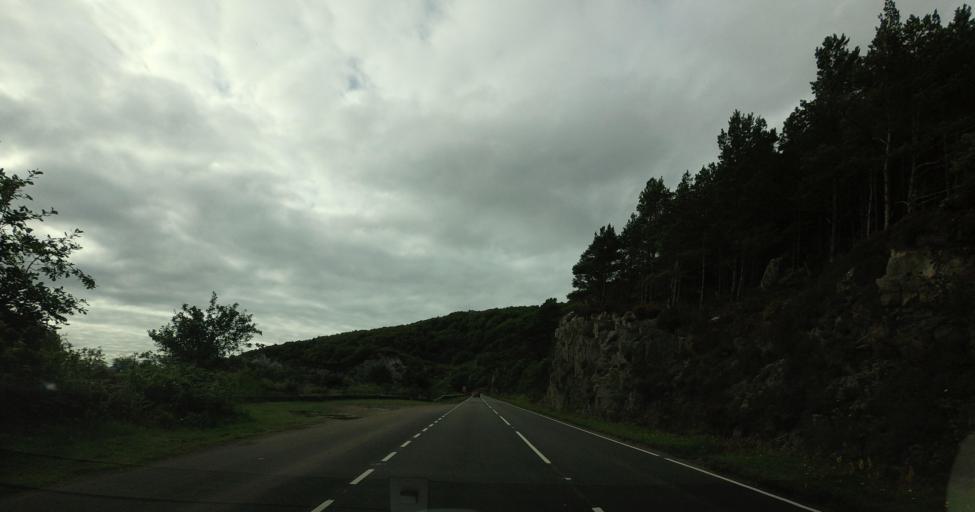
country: GB
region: Scotland
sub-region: Highland
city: Portree
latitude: 57.2799
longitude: -5.6863
